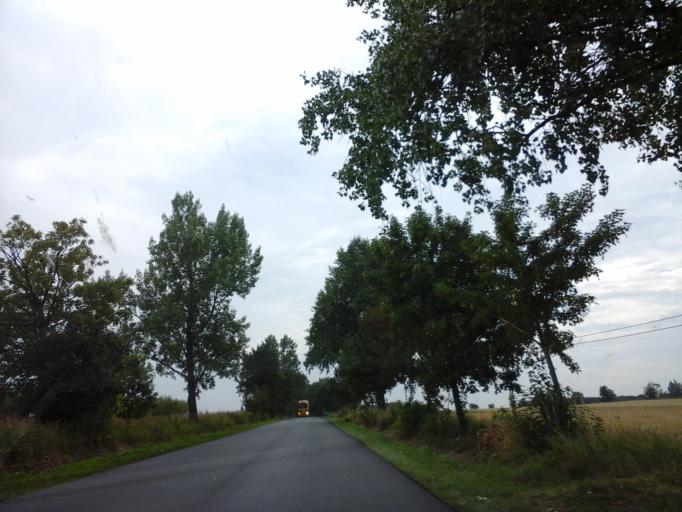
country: PL
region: Lower Silesian Voivodeship
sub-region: Powiat zabkowicki
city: Cieplowody
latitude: 50.6467
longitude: 16.8939
